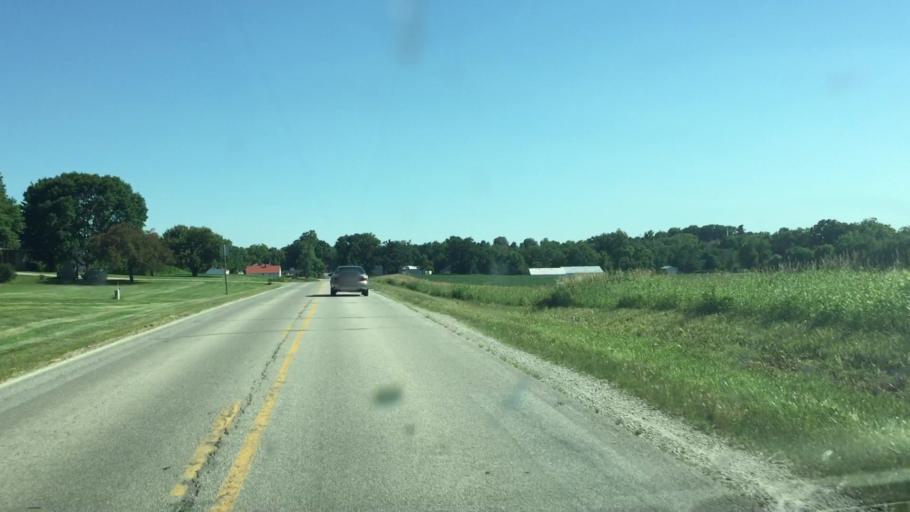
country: US
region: Iowa
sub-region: Linn County
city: Ely
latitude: 41.8555
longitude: -91.6463
